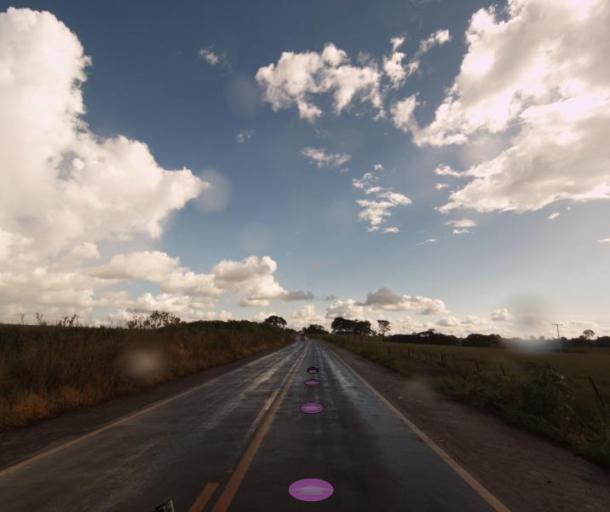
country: BR
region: Goias
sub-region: Itaberai
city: Itaberai
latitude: -16.0179
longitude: -49.7725
